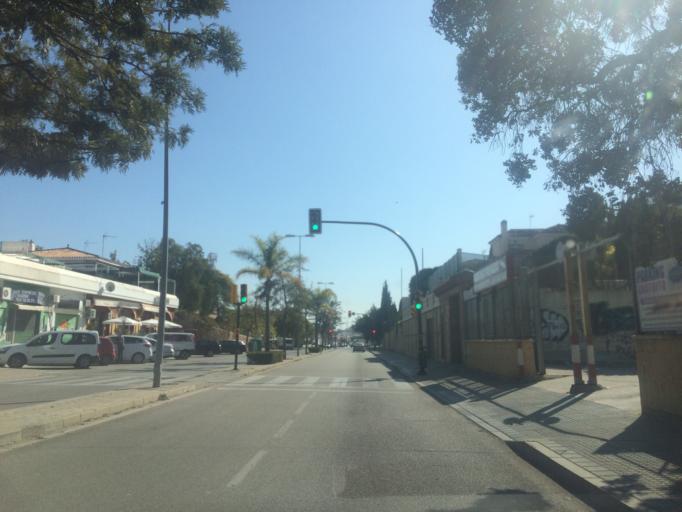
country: ES
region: Andalusia
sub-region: Provincia de Malaga
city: Malaga
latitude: 36.7443
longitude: -4.4908
